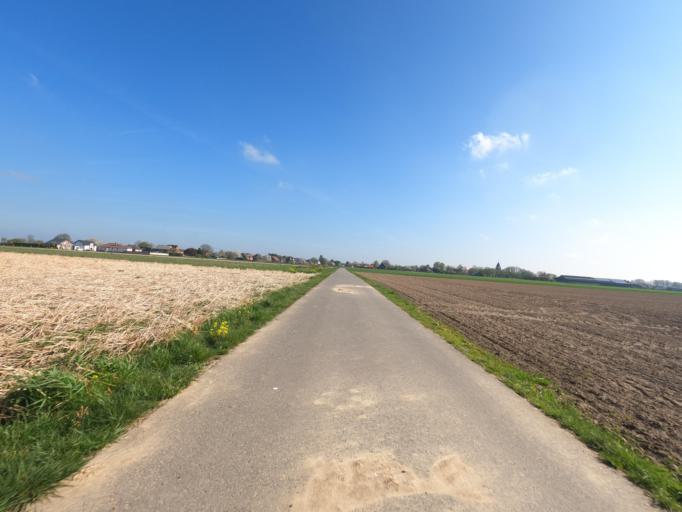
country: DE
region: North Rhine-Westphalia
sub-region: Regierungsbezirk Koln
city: Heinsberg
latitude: 51.0347
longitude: 6.0491
